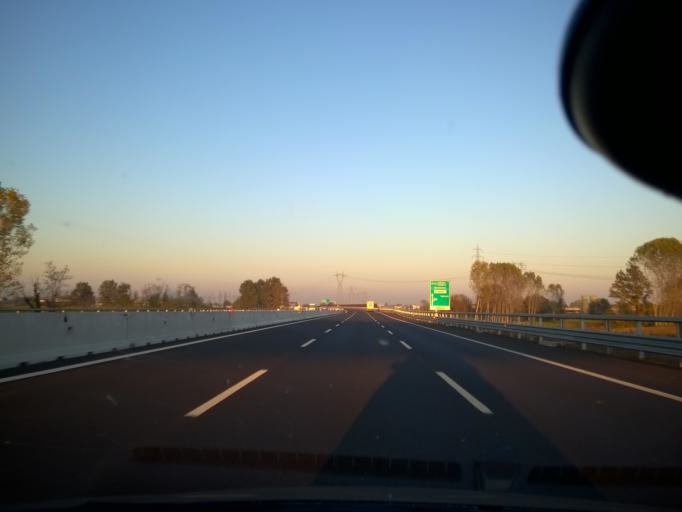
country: IT
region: Lombardy
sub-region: Citta metropolitana di Milano
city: Paullo
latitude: 45.4077
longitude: 9.4075
